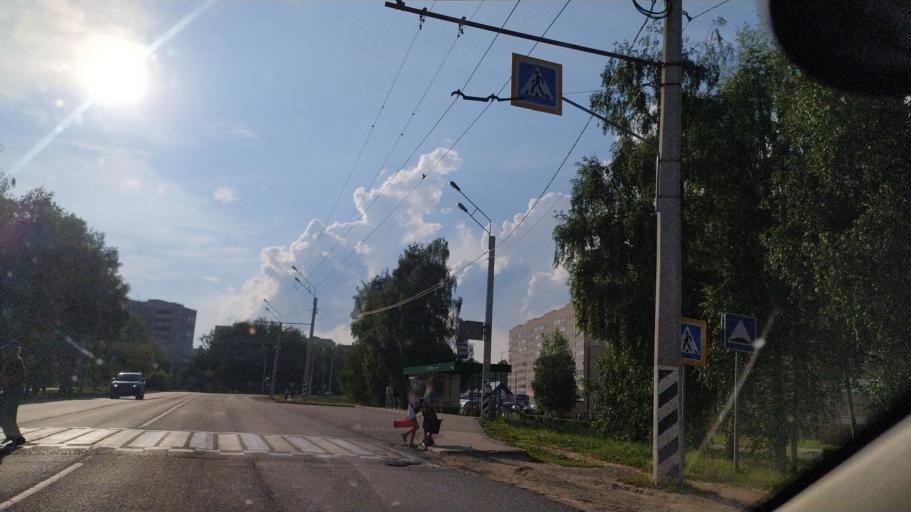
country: RU
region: Chuvashia
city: Novocheboksarsk
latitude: 56.1104
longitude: 47.4476
